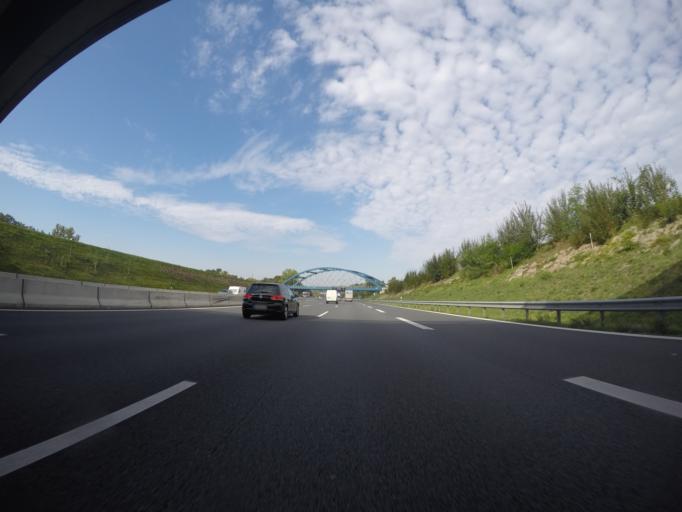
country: DE
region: Bavaria
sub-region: Regierungsbezirk Unterfranken
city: Sailauf
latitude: 50.0010
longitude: 9.2356
